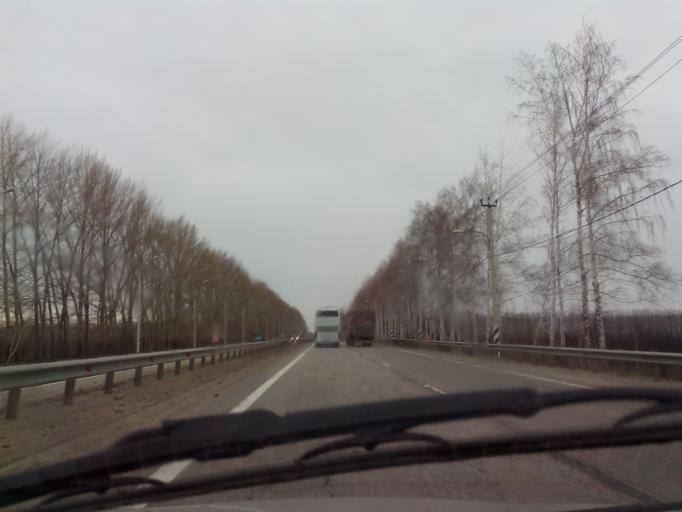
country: RU
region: Tambov
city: Selezni
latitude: 52.7545
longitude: 41.1665
